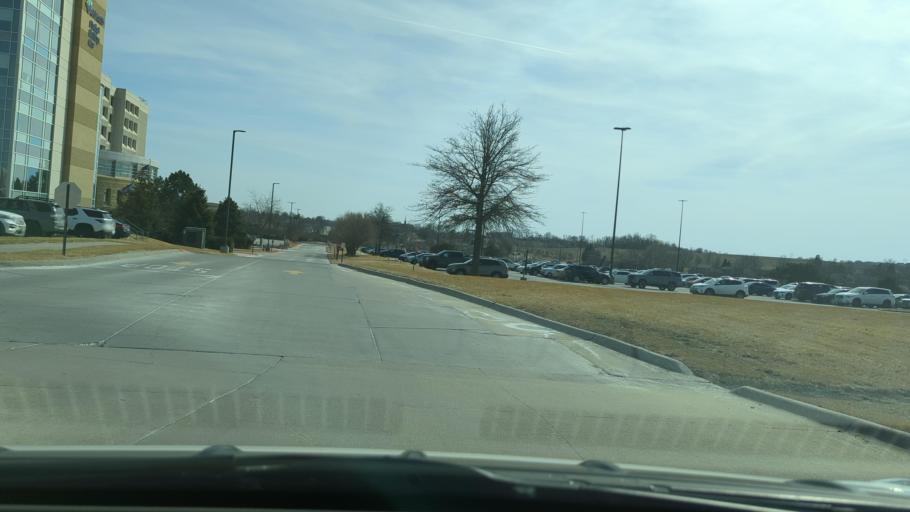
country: US
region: Nebraska
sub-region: Sarpy County
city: Papillion
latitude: 41.1371
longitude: -96.0411
